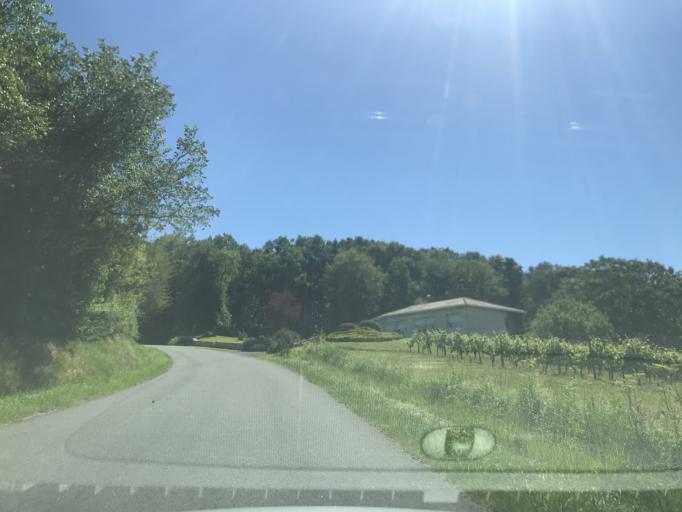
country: FR
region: Poitou-Charentes
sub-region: Departement de la Charente-Maritime
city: Mortagne-sur-Gironde
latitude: 45.4142
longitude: -0.7063
